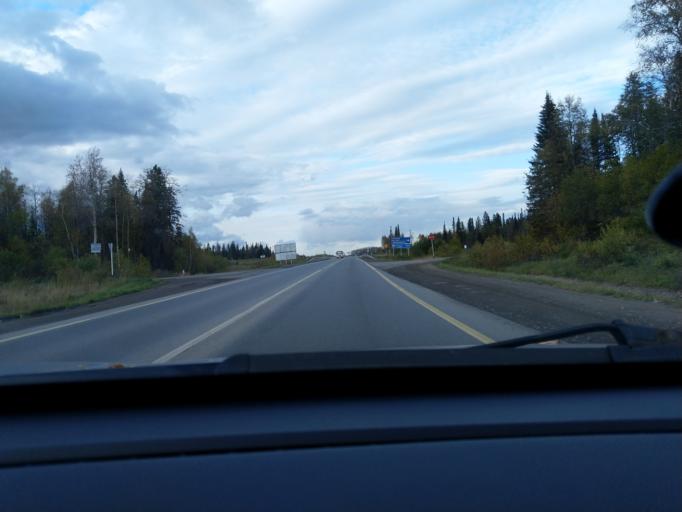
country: RU
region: Perm
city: Polazna
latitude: 58.2921
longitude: 56.4797
